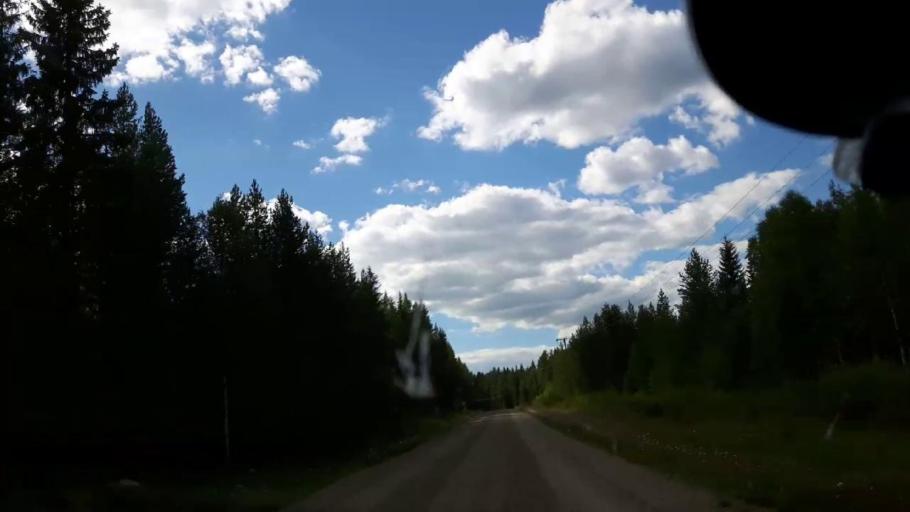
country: SE
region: Vaesternorrland
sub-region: Ange Kommun
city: Ange
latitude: 62.7685
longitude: 15.7680
